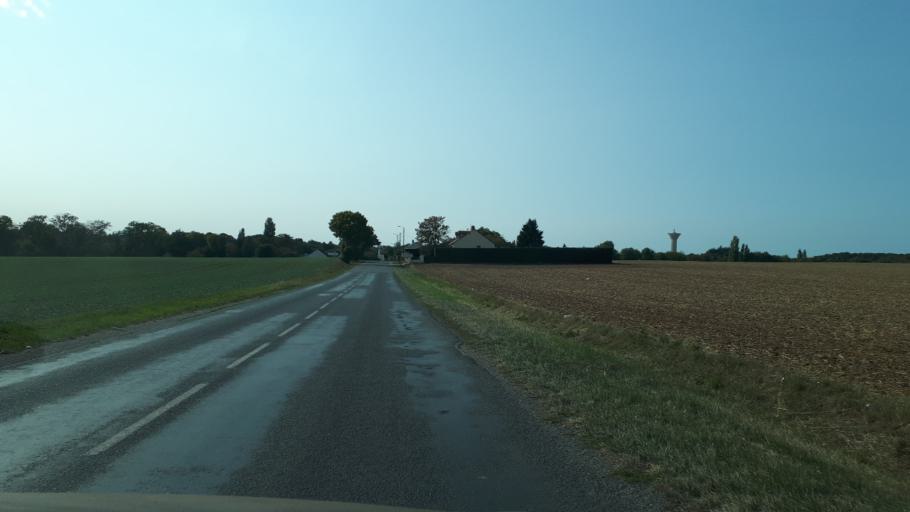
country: FR
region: Centre
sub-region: Departement du Cher
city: Rians
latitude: 47.1967
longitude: 2.5892
